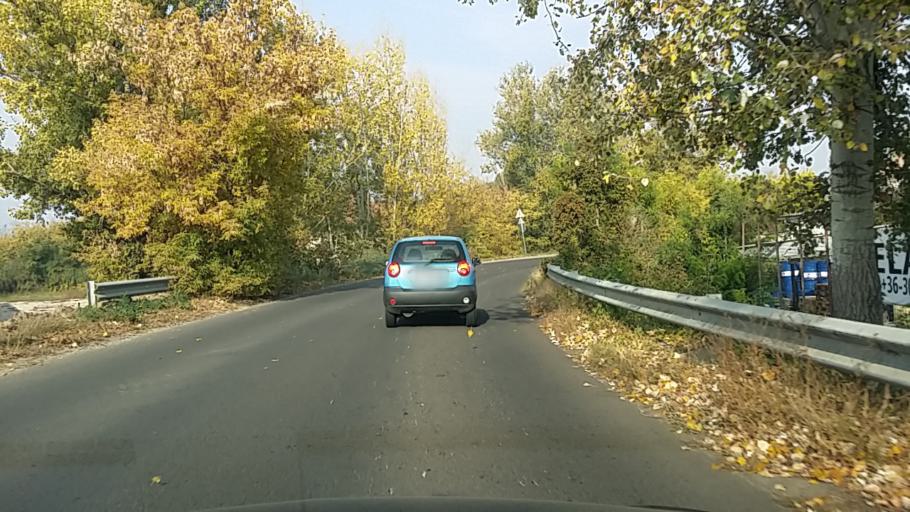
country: HU
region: Pest
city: Dunakeszi
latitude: 47.6017
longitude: 19.1506
